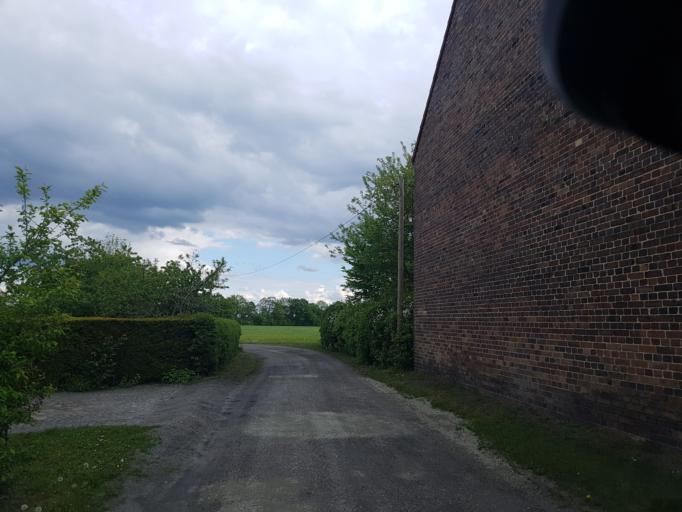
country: DE
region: Brandenburg
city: Grossraschen
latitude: 51.5859
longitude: 14.0595
